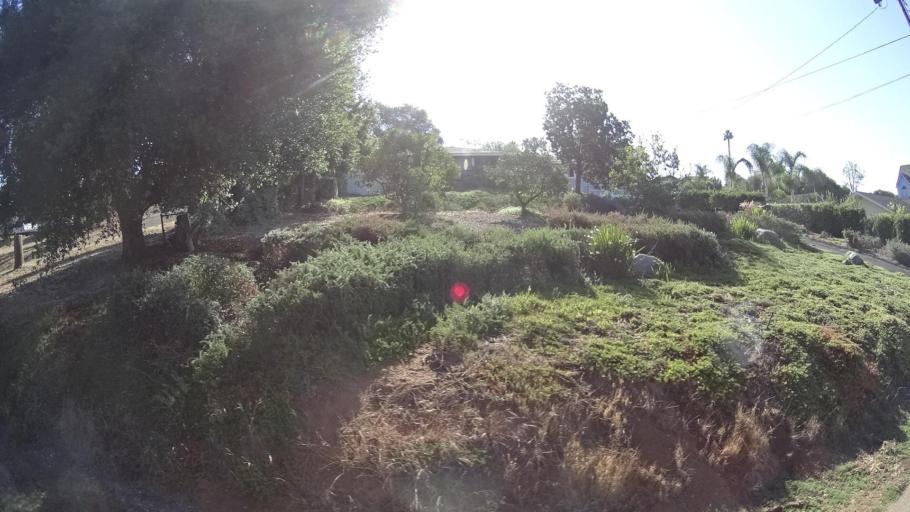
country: US
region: California
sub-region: San Diego County
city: Escondido
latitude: 33.0807
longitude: -117.0785
